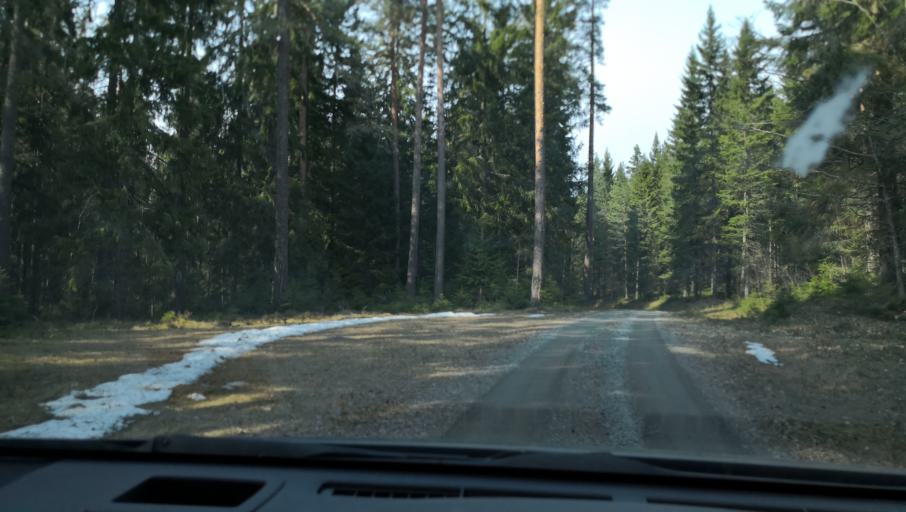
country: SE
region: OErebro
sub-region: Lindesbergs Kommun
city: Frovi
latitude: 59.3780
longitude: 15.4193
